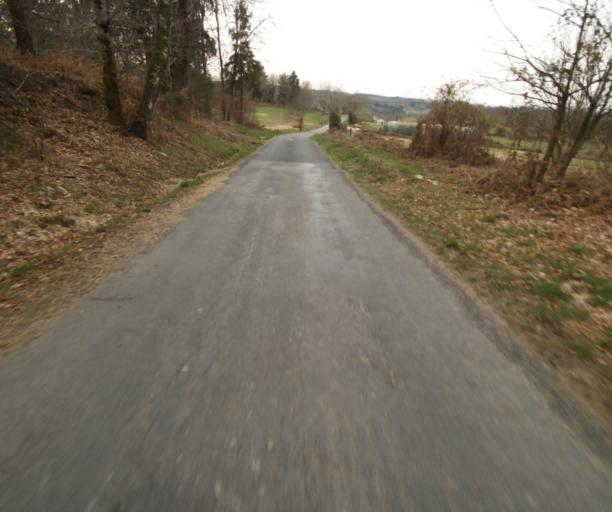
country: FR
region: Limousin
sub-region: Departement de la Correze
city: Correze
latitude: 45.4402
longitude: 1.8221
